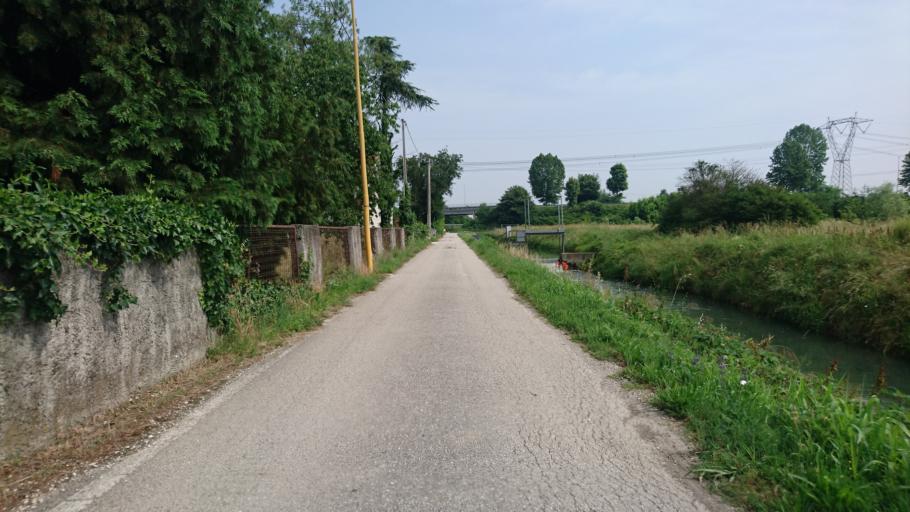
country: IT
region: Veneto
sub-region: Provincia di Padova
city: Ponte San Nicolo
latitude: 45.3570
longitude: 11.9434
